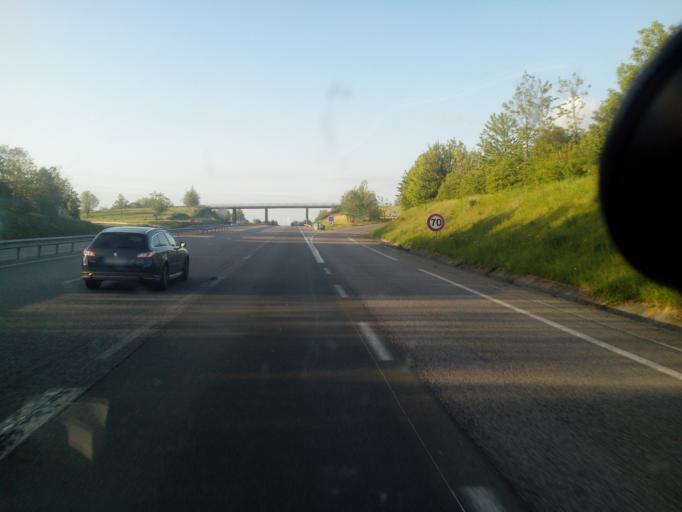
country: FR
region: Haute-Normandie
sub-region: Departement de la Seine-Maritime
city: Neufchatel-en-Bray
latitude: 49.7412
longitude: 1.4724
